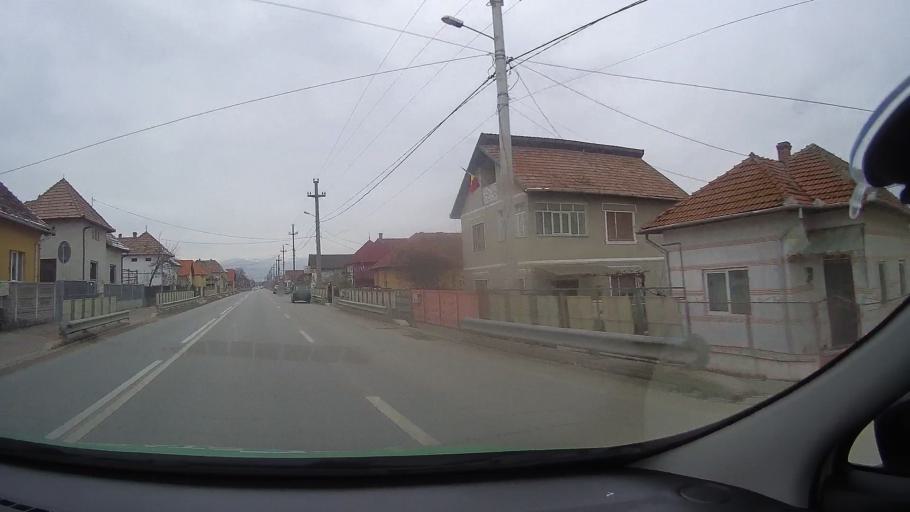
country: RO
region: Alba
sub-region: Municipiul Alba Iulia
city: Micesti
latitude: 46.1007
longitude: 23.5499
